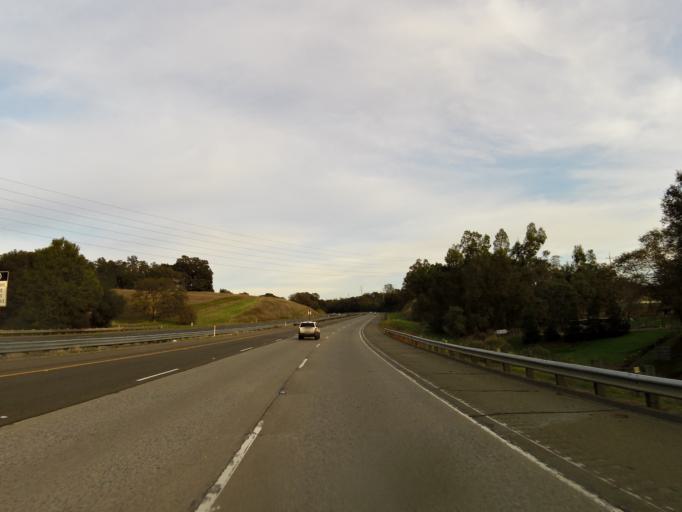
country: US
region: California
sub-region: El Dorado County
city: Cameron Park
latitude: 38.6574
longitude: -120.9918
